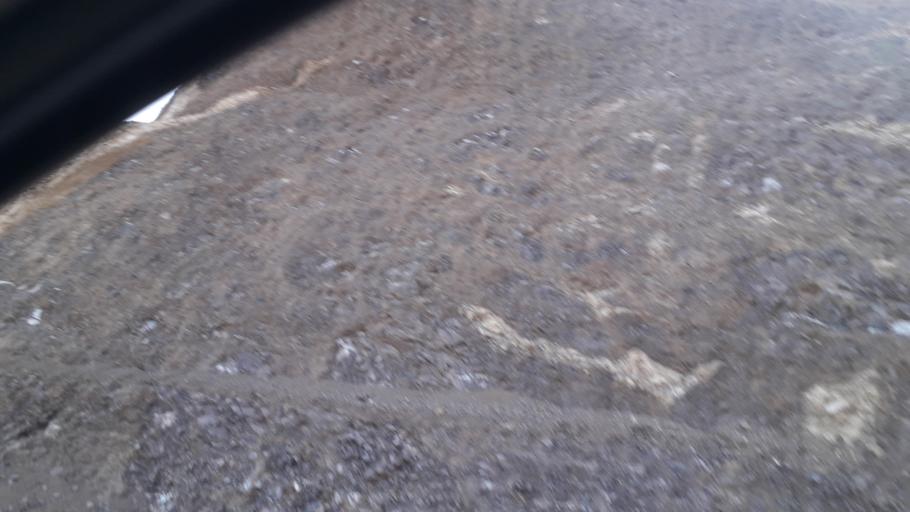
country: ET
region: Amhara
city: Dese
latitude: 11.5206
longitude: 39.2501
